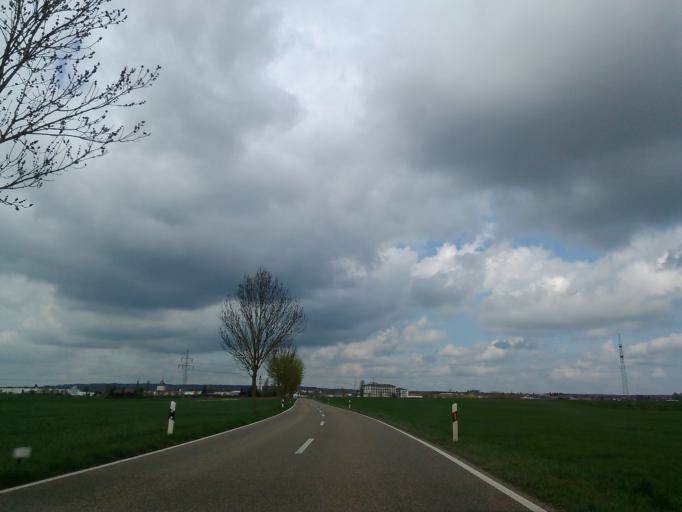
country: DE
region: Baden-Wuerttemberg
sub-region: Tuebingen Region
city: Langenau
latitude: 48.4877
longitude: 10.1383
